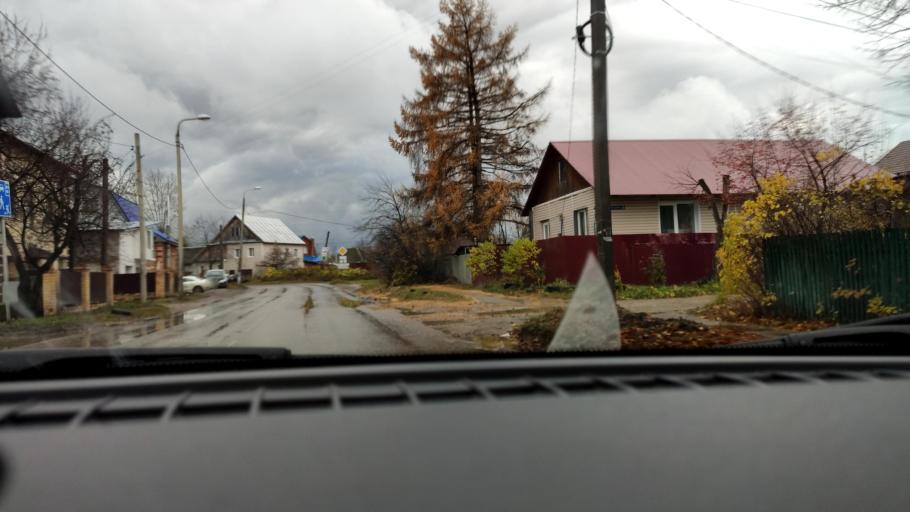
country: RU
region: Perm
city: Perm
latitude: 58.0184
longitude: 56.3143
